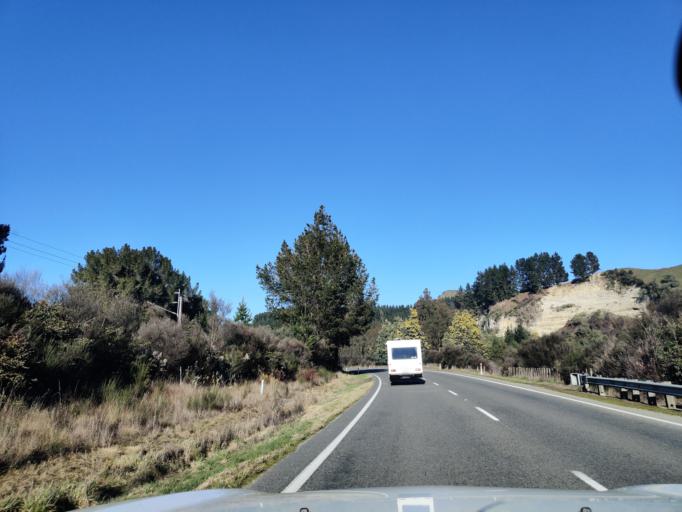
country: NZ
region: Manawatu-Wanganui
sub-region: Ruapehu District
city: Waiouru
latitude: -39.7544
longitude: 175.8308
